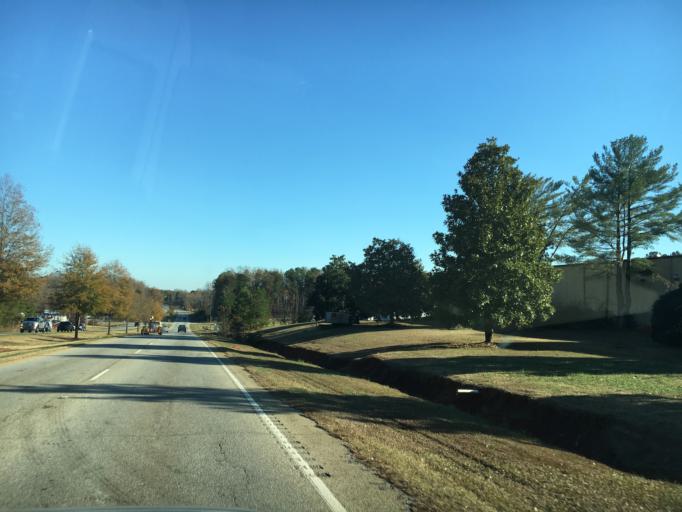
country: US
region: South Carolina
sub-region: Spartanburg County
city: Wellford
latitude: 34.9440
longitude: -82.0891
